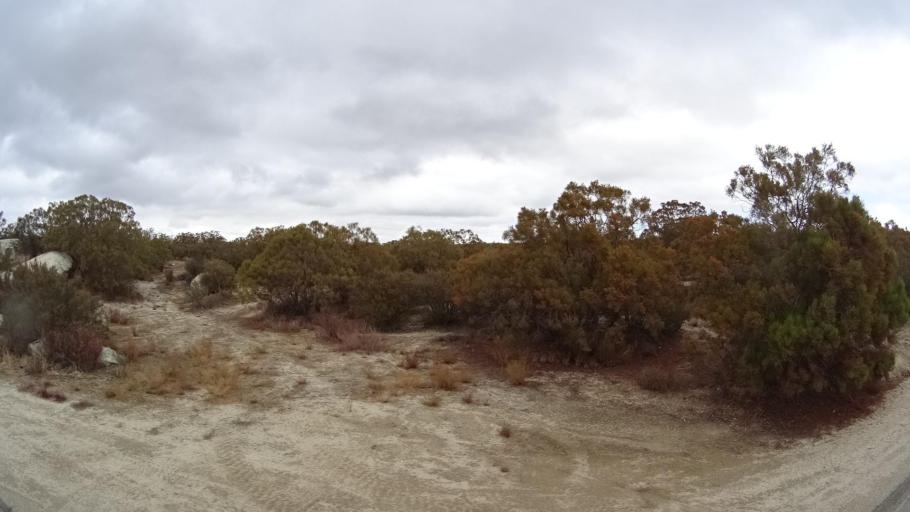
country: US
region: California
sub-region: San Diego County
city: Campo
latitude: 32.6052
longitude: -116.3405
